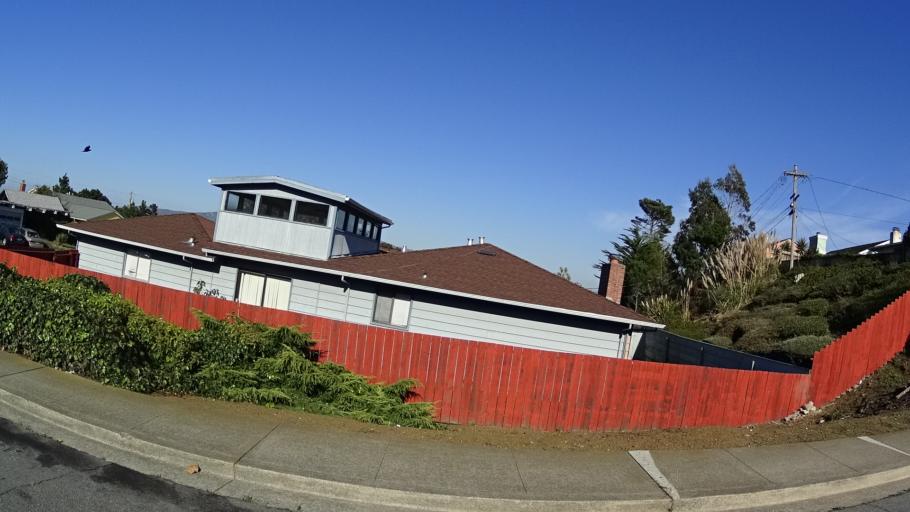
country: US
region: California
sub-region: San Mateo County
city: Pacifica
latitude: 37.6331
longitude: -122.4538
